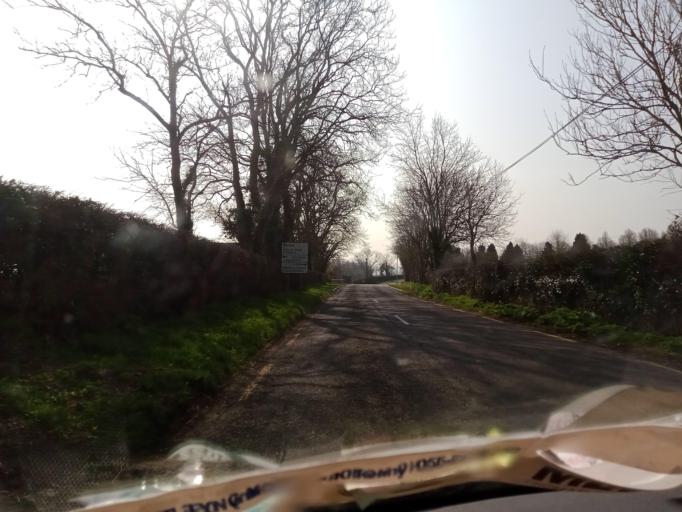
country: IE
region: Leinster
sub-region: Kilkenny
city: Callan
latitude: 52.5011
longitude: -7.3814
